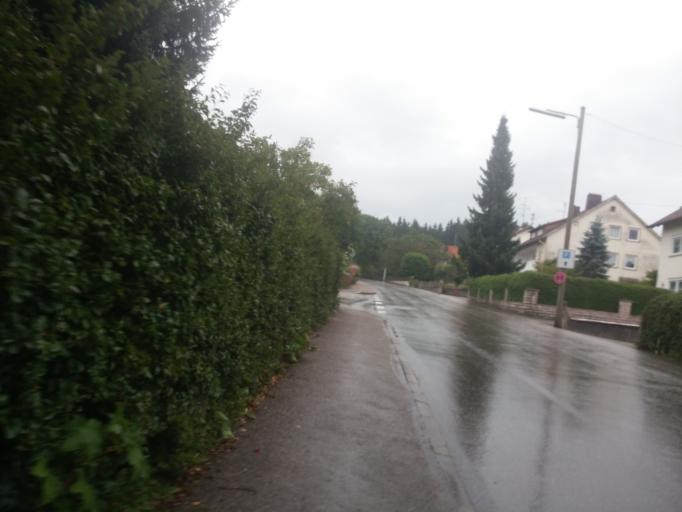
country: DE
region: Bavaria
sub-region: Swabia
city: Woringen
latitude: 47.8710
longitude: 10.2212
